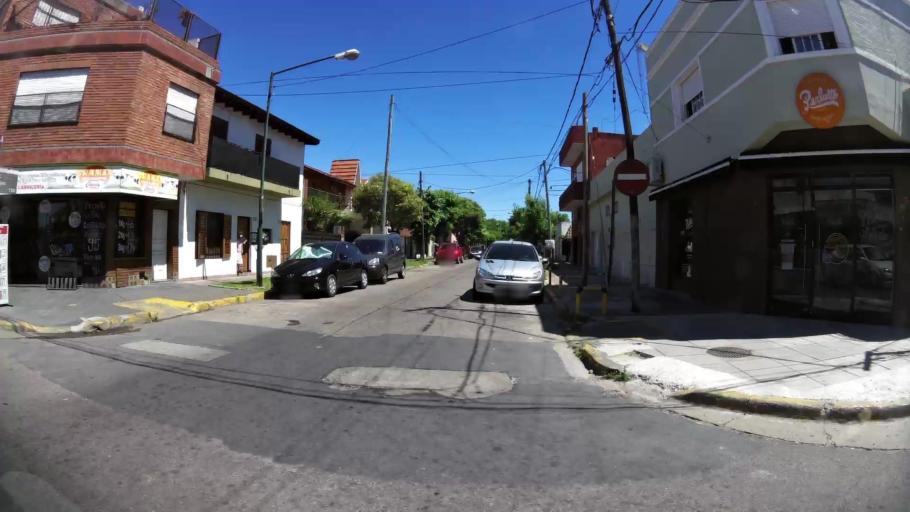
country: AR
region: Buenos Aires
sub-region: Partido de General San Martin
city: General San Martin
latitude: -34.5295
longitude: -58.5531
